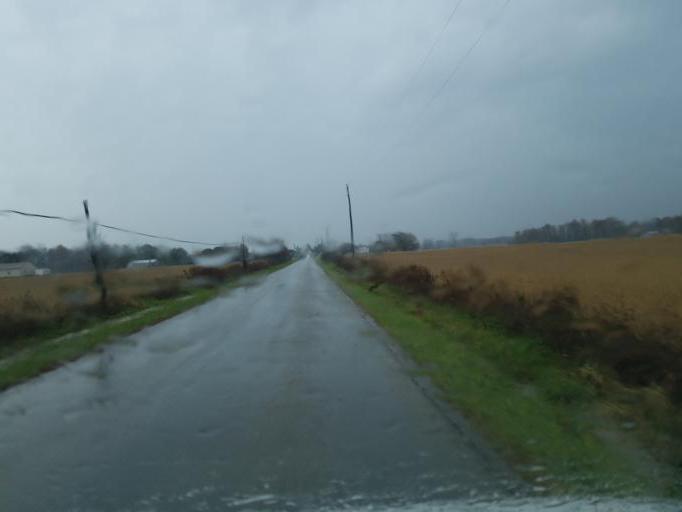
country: US
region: Ohio
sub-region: Morrow County
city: Cardington
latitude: 40.4660
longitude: -82.8737
